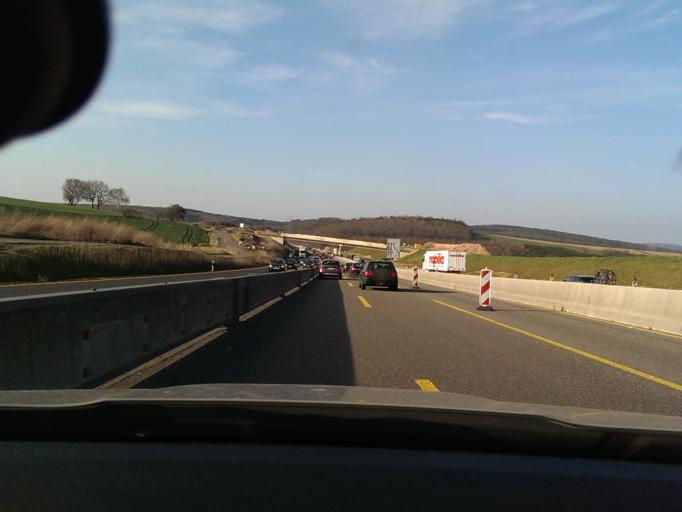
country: DE
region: Hesse
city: Felsberg
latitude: 51.1349
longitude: 9.4742
